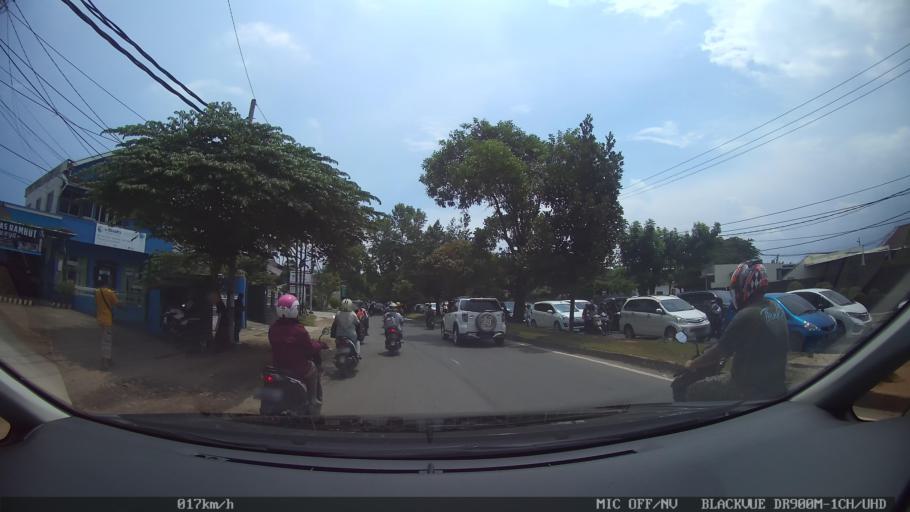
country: ID
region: Lampung
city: Kedaton
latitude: -5.3807
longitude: 105.2717
